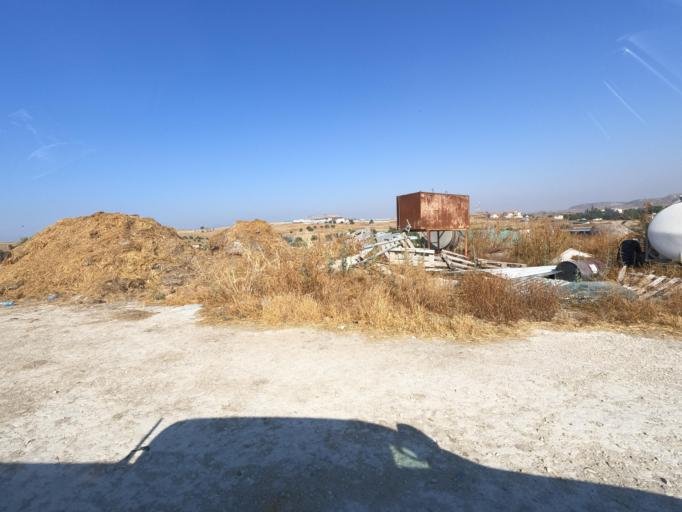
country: CY
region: Lefkosia
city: Lympia
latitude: 34.9869
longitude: 33.4702
